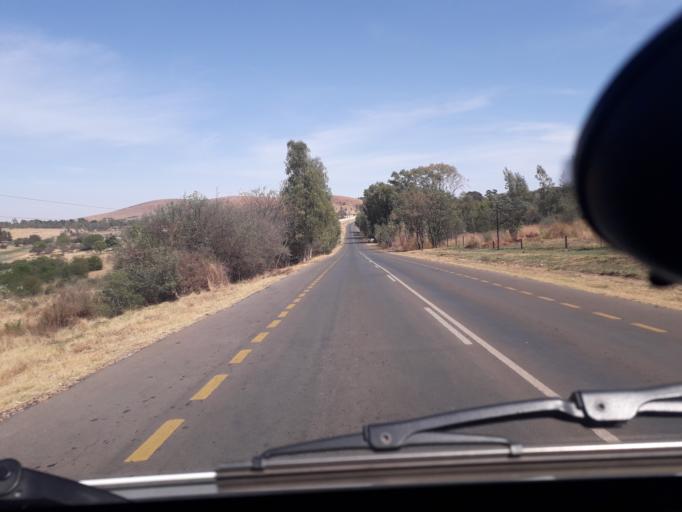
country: ZA
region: Gauteng
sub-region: West Rand District Municipality
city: Muldersdriseloop
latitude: -25.9896
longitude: 27.8312
